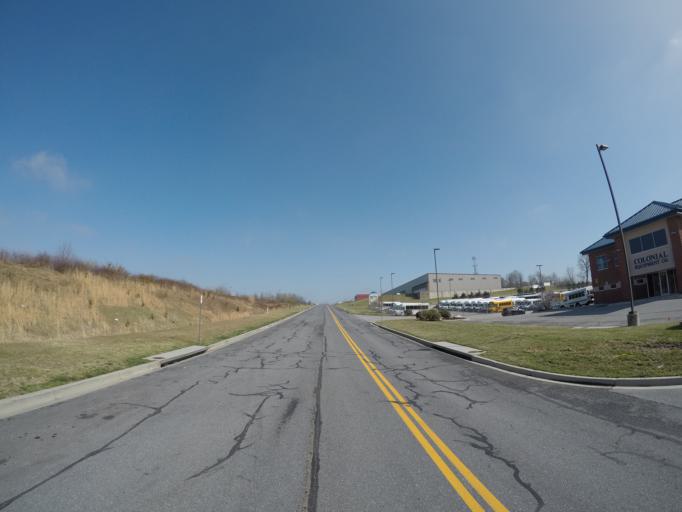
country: US
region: Maryland
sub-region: Frederick County
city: Green Valley
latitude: 39.3751
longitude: -77.2766
